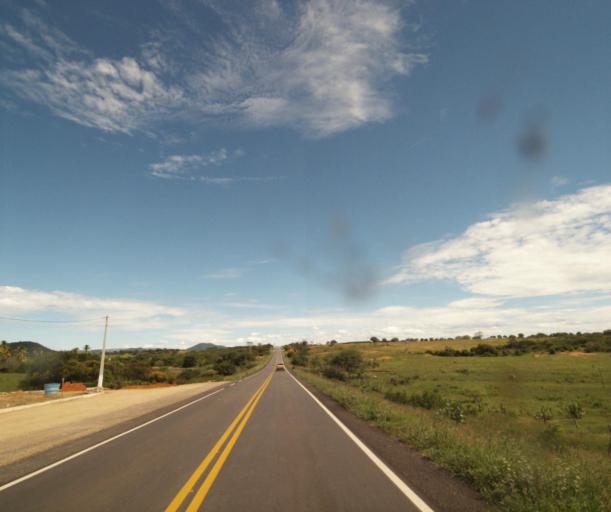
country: BR
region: Bahia
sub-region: Guanambi
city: Guanambi
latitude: -14.3771
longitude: -42.7727
